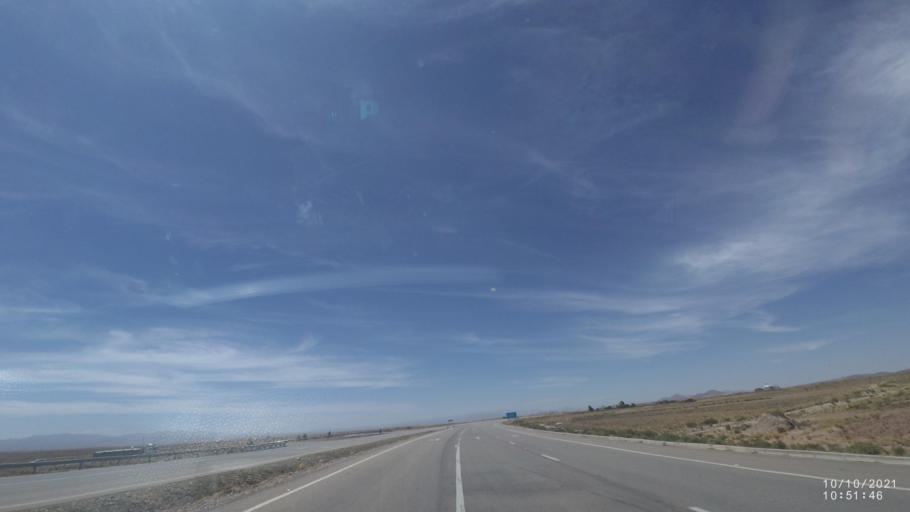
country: BO
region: La Paz
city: Colquiri
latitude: -17.6559
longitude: -67.2092
